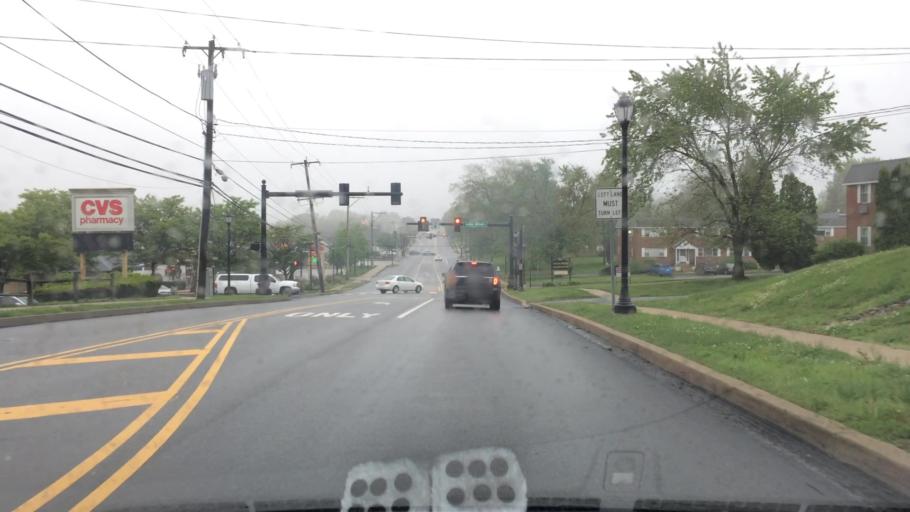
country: US
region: Pennsylvania
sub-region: Delaware County
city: Village Green-Green Ridge
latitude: 39.8667
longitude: -75.4283
